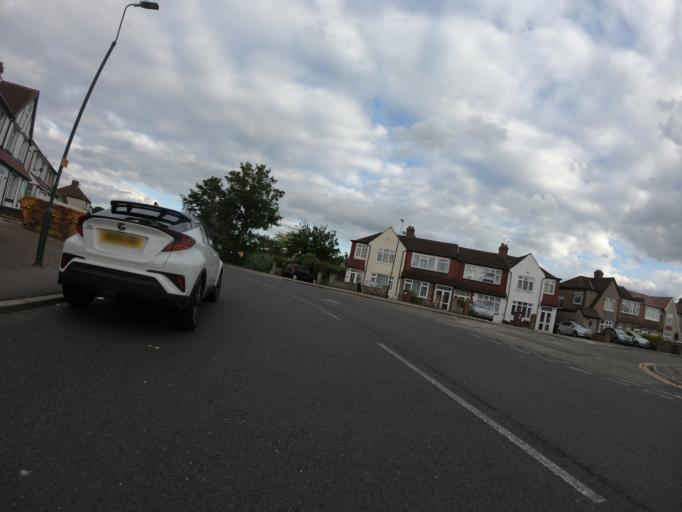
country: GB
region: England
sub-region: Greater London
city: Bexleyheath
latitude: 51.4804
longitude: 0.1327
